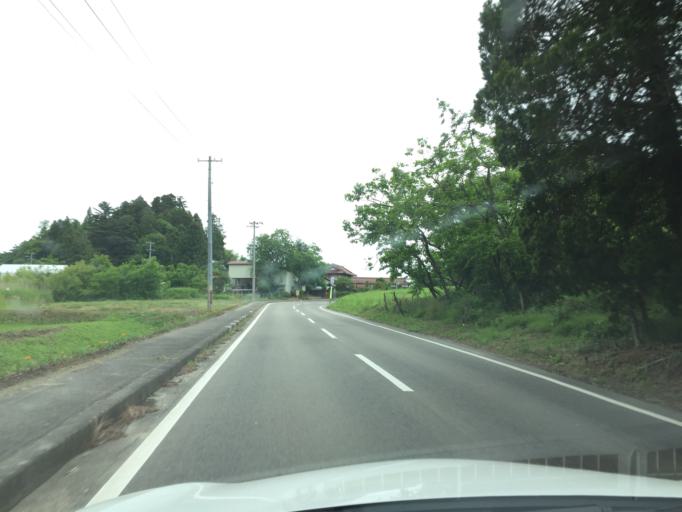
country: JP
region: Fukushima
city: Funehikimachi-funehiki
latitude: 37.4133
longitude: 140.5462
